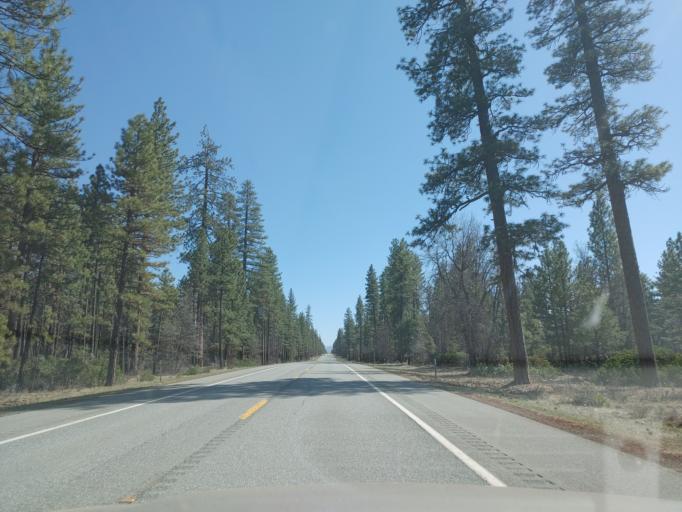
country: US
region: California
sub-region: Shasta County
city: Burney
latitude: 40.9786
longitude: -121.6224
